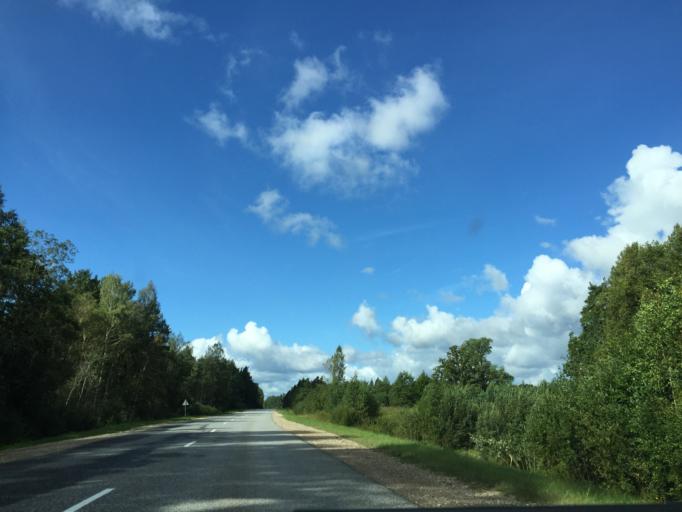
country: LV
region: Kuldigas Rajons
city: Kuldiga
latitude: 56.9827
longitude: 22.0464
